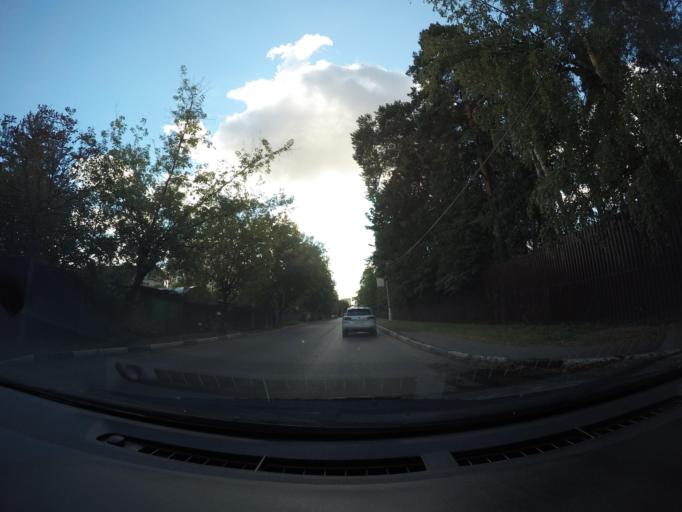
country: RU
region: Moskovskaya
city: Kratovo
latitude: 55.5848
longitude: 38.1957
